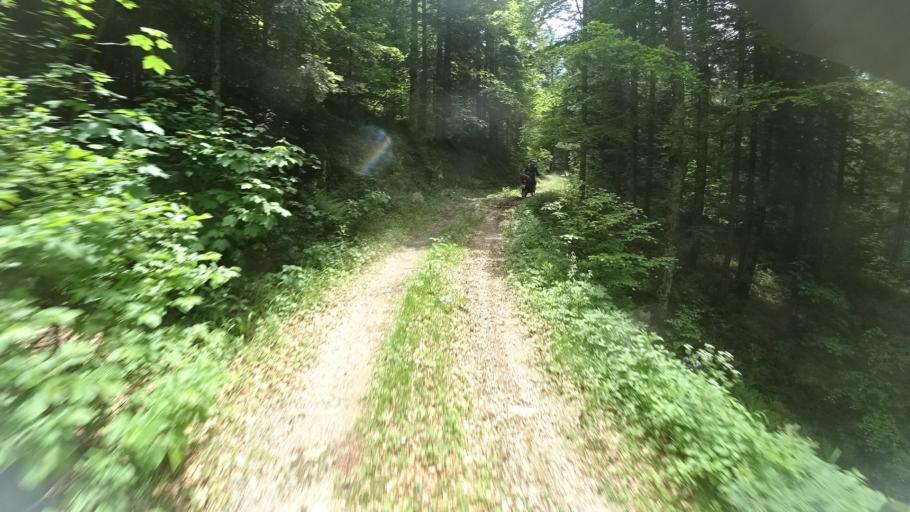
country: HR
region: Zadarska
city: Gracac
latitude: 44.4773
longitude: 15.8939
